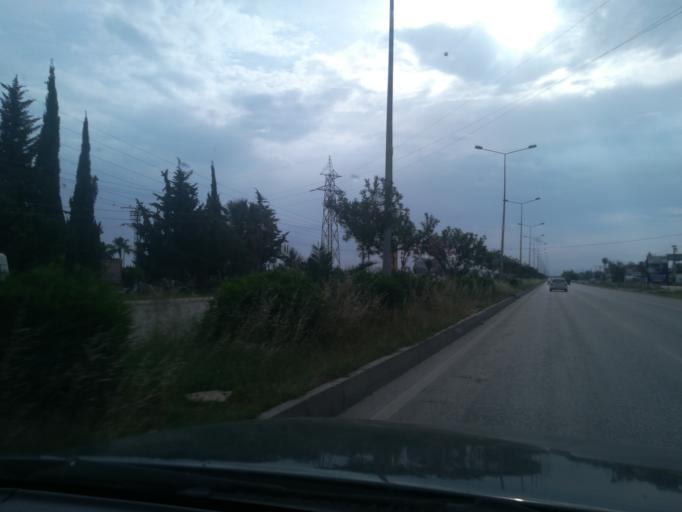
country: TR
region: Adana
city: Yuregir
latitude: 36.9827
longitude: 35.4104
